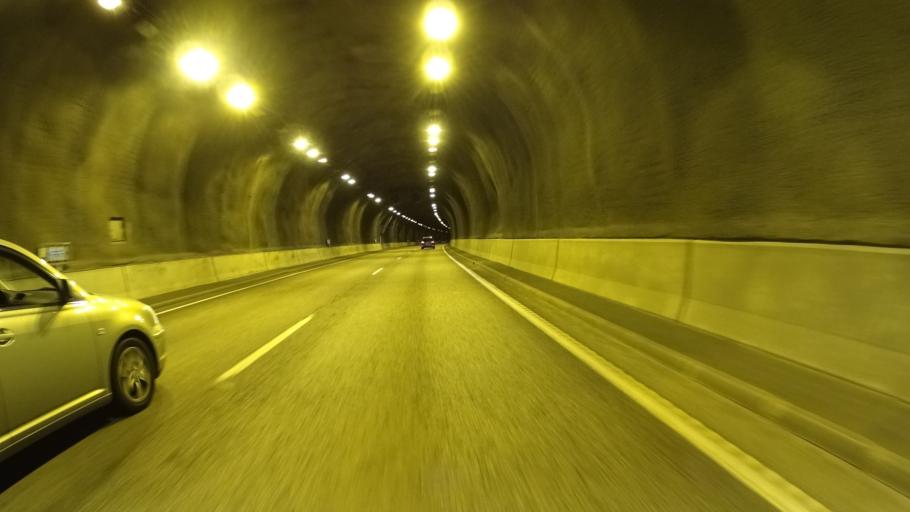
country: FI
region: Uusimaa
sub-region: Helsinki
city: Vantaa
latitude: 60.2390
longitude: 25.1579
